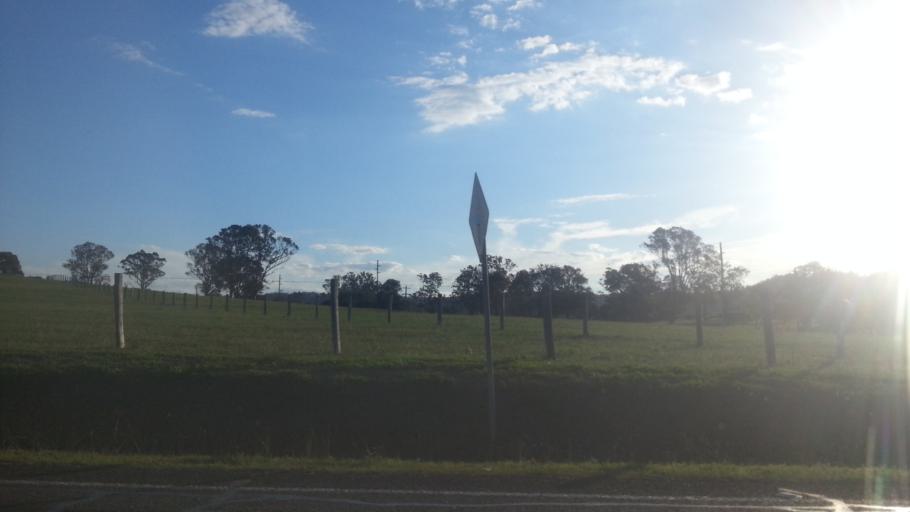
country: AU
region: New South Wales
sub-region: Wollondilly
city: Douglas Park
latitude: -34.1408
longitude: 150.7149
